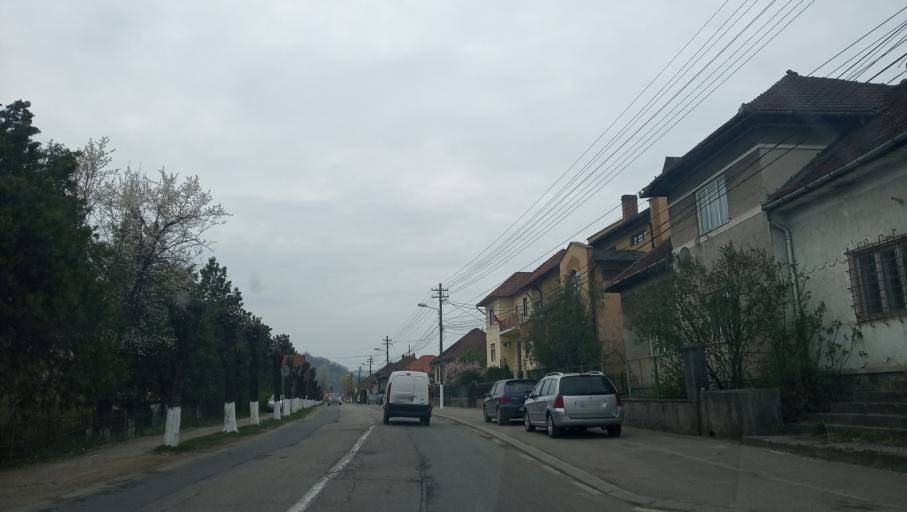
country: RO
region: Hunedoara
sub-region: Municipiul Brad
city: Brad
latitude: 46.1222
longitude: 22.7893
